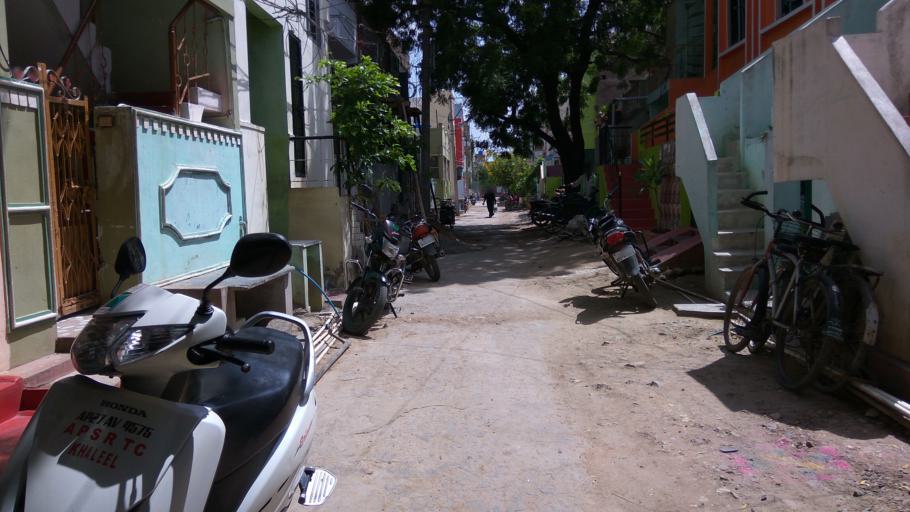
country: IN
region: Andhra Pradesh
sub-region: Prakasam
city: Markapur
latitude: 15.7446
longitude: 79.2714
